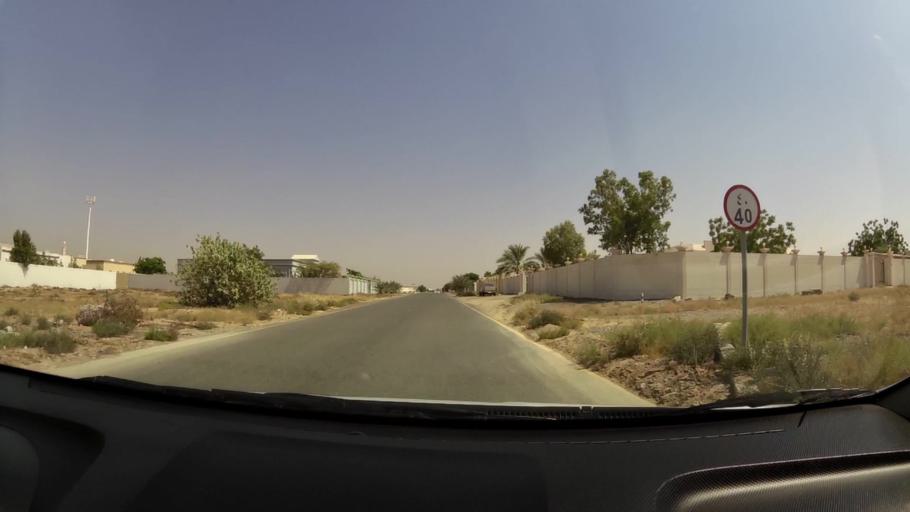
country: AE
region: Umm al Qaywayn
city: Umm al Qaywayn
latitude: 25.4928
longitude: 55.5861
